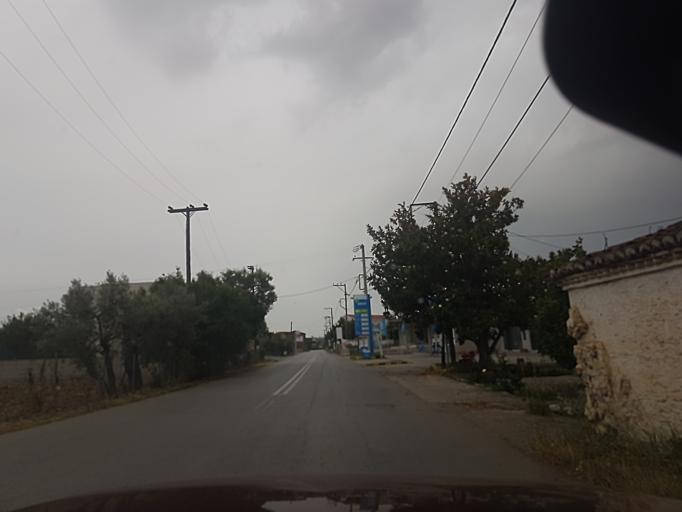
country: GR
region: Central Greece
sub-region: Nomos Evvoias
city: Mytikas
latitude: 38.4643
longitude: 23.6341
